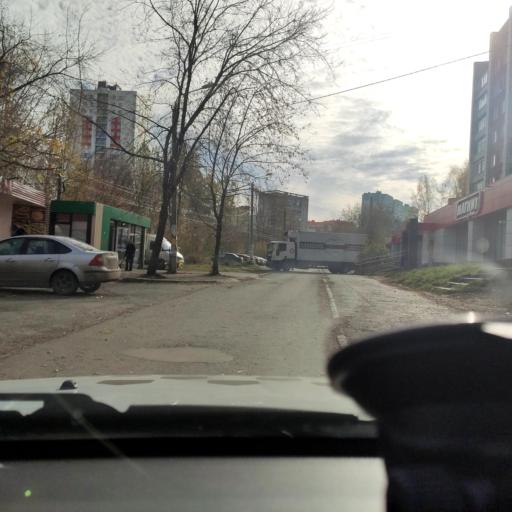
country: RU
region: Perm
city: Perm
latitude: 57.9985
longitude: 56.2166
